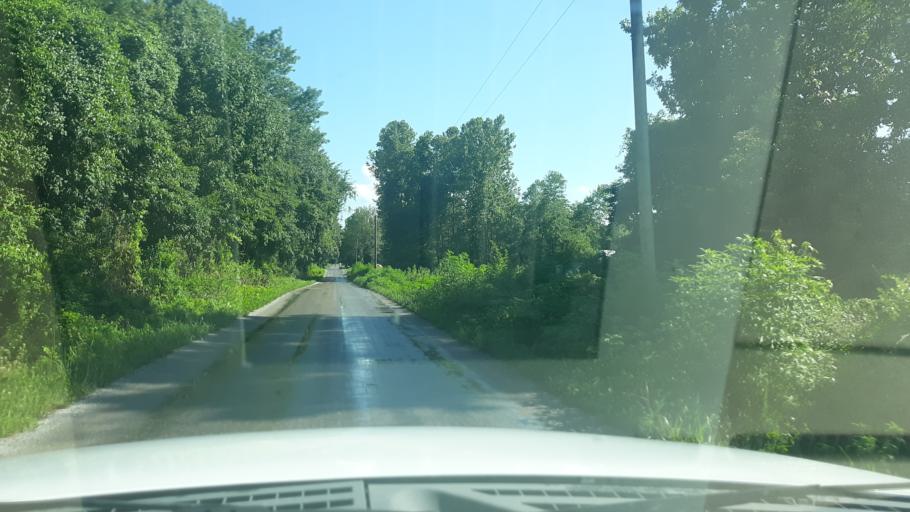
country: US
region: Illinois
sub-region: Saline County
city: Harrisburg
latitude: 37.8601
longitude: -88.5814
